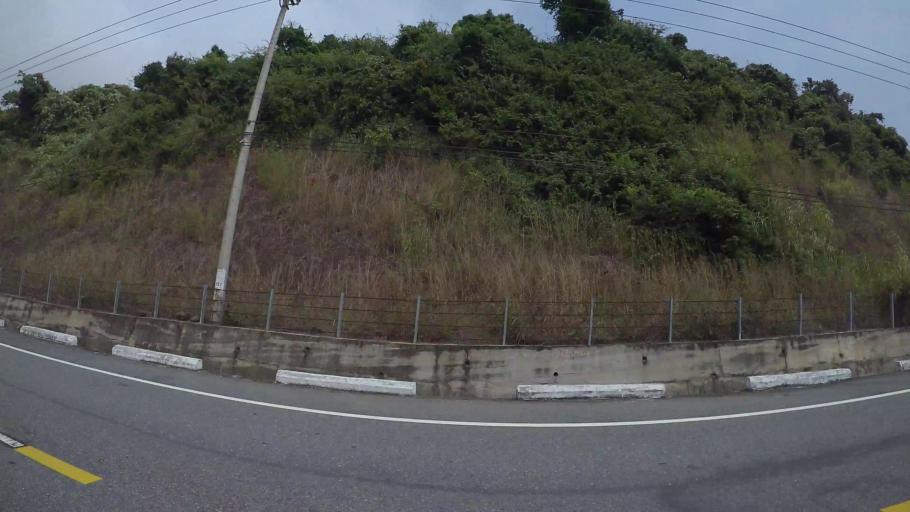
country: VN
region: Da Nang
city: Son Tra
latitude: 16.0985
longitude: 108.3044
